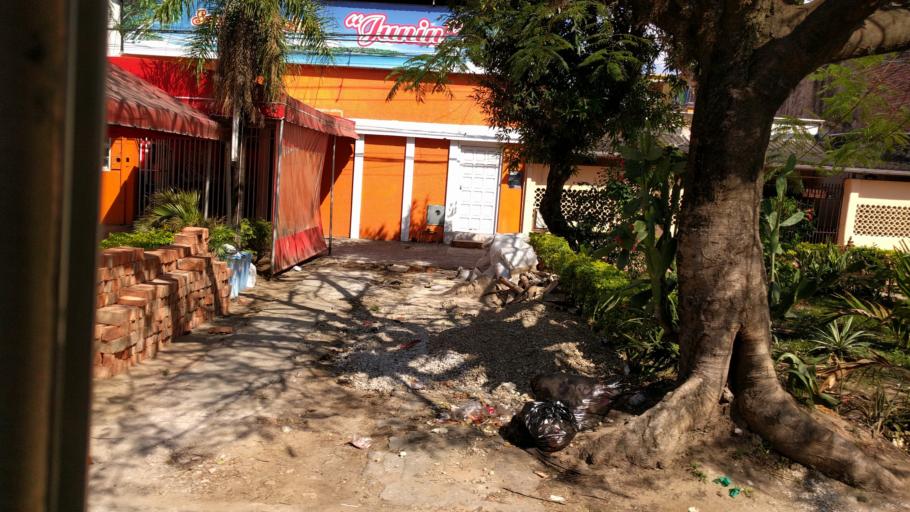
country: BO
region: Santa Cruz
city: Santa Cruz de la Sierra
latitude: -17.7833
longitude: -63.1936
